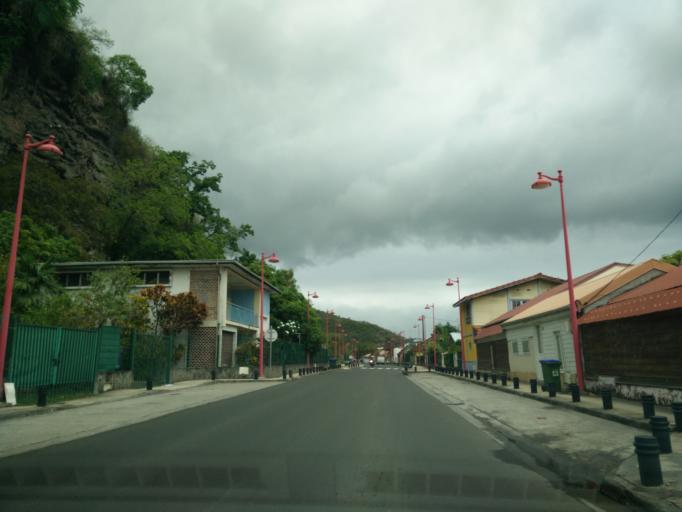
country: MQ
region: Martinique
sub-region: Martinique
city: Saint-Pierre
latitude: 14.7035
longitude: -61.1822
